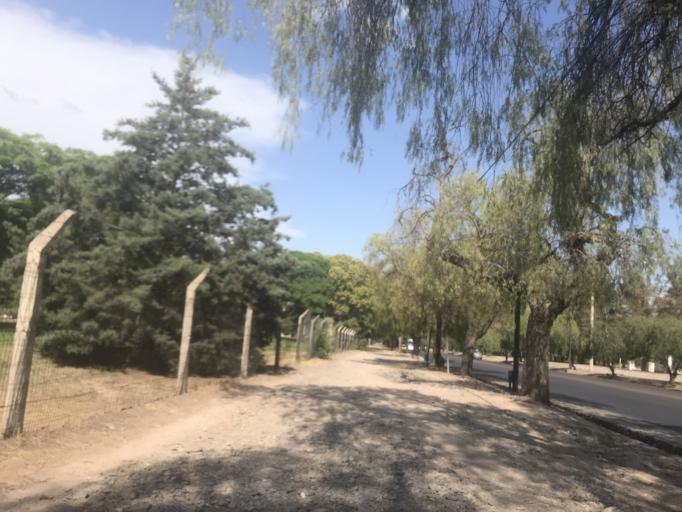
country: AR
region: Mendoza
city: Mendoza
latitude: -32.8833
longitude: -68.8784
